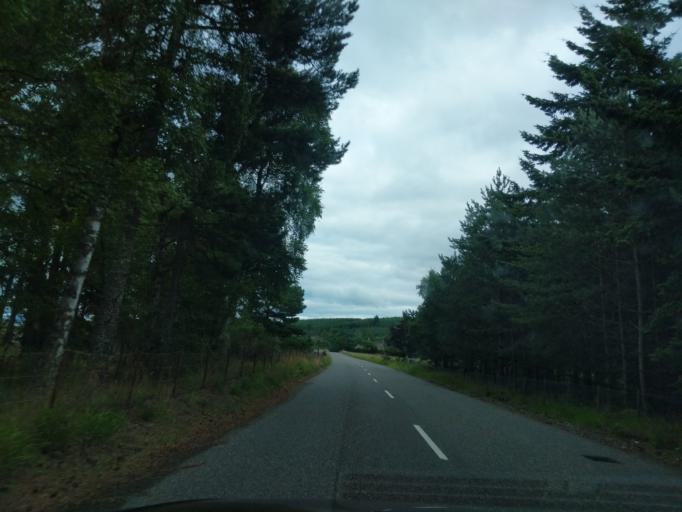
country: GB
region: Scotland
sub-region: Aberdeenshire
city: Aboyne
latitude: 57.0706
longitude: -2.8605
